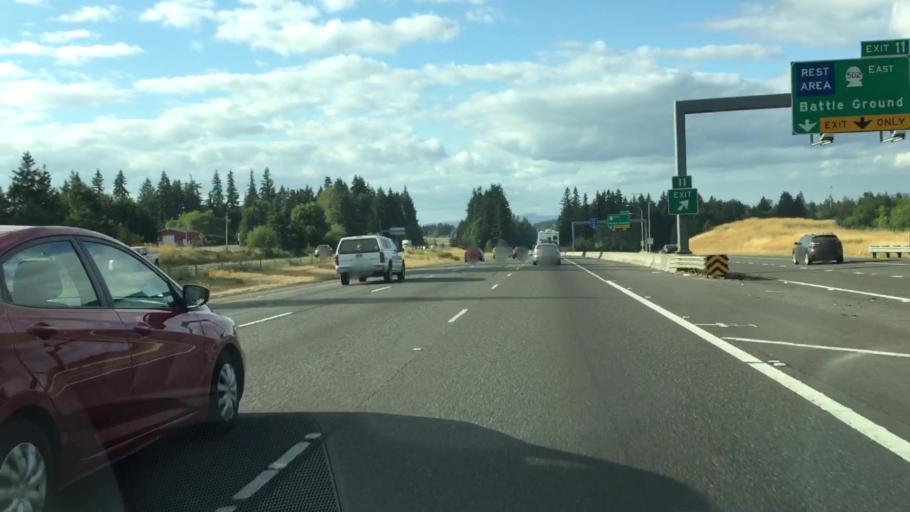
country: US
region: Washington
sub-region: Clark County
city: Mount Vista
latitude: 45.7694
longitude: -122.6687
